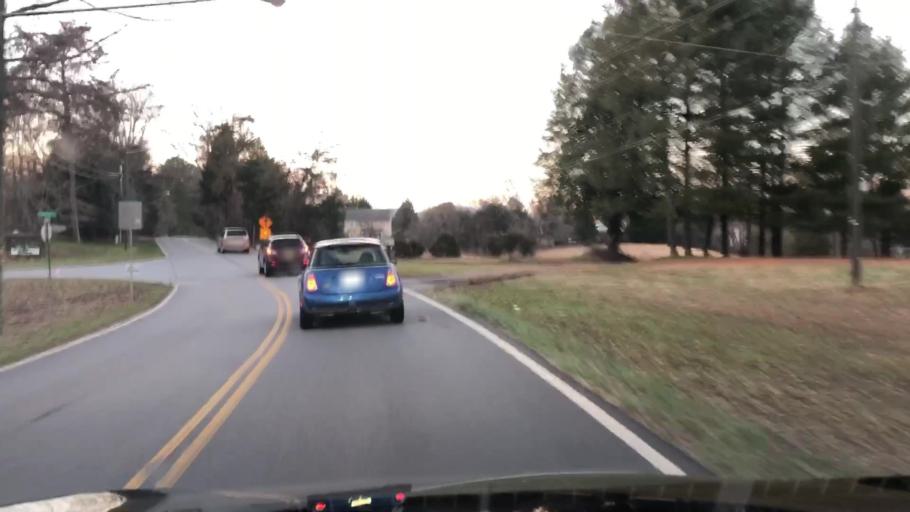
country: US
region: Virginia
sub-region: City of Lynchburg
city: West Lynchburg
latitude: 37.4210
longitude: -79.2442
